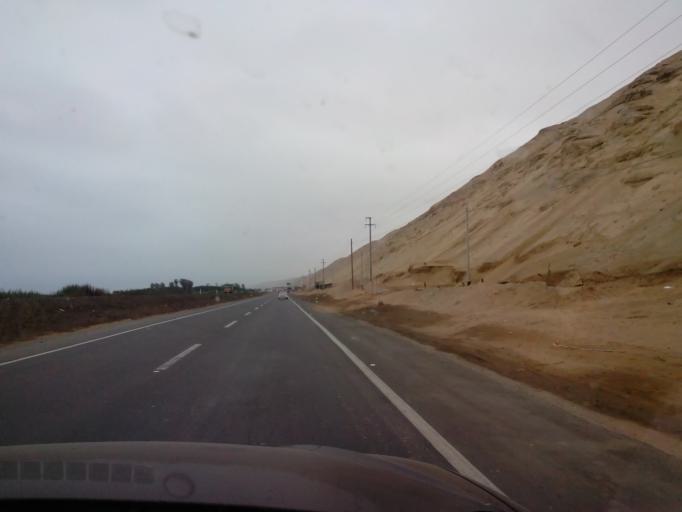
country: PE
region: Ica
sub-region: Provincia de Chincha
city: San Pedro
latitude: -13.3947
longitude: -76.1980
